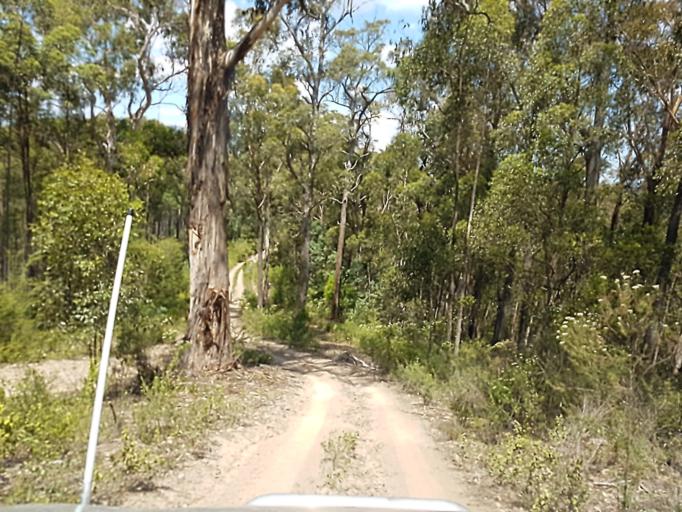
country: AU
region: Victoria
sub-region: East Gippsland
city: Lakes Entrance
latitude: -37.4059
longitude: 148.3024
